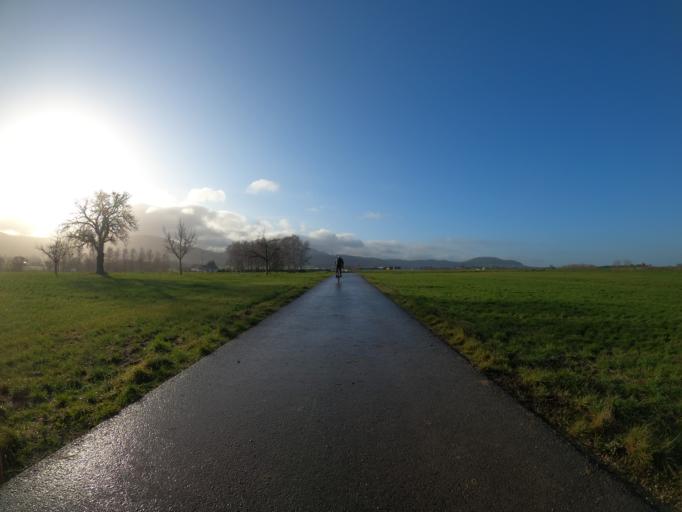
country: DE
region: Baden-Wuerttemberg
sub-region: Regierungsbezirk Stuttgart
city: Boll
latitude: 48.6551
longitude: 9.6207
